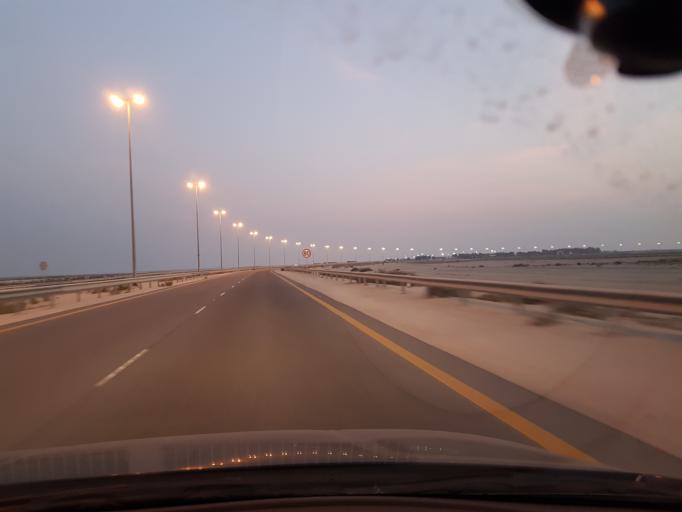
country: BH
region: Central Governorate
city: Dar Kulayb
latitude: 26.0020
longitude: 50.4851
